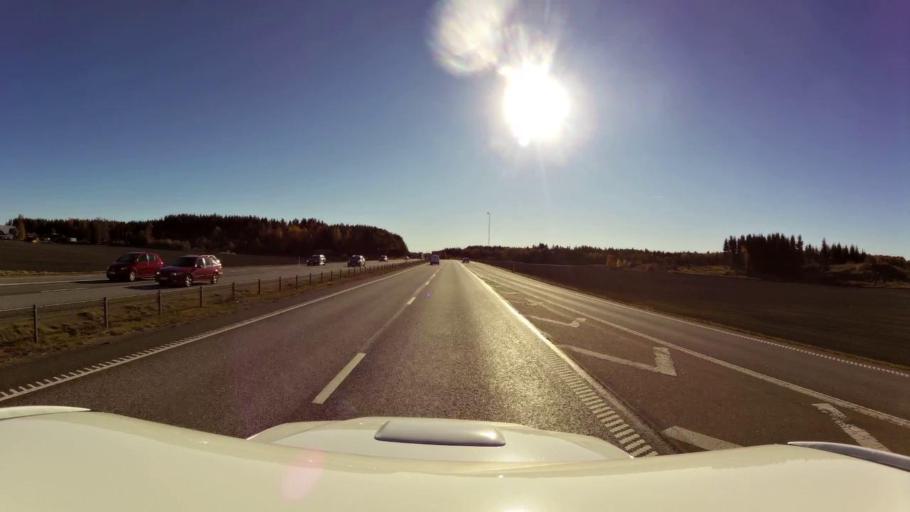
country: SE
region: OEstergoetland
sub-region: Linkopings Kommun
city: Malmslatt
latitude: 58.4233
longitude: 15.5383
